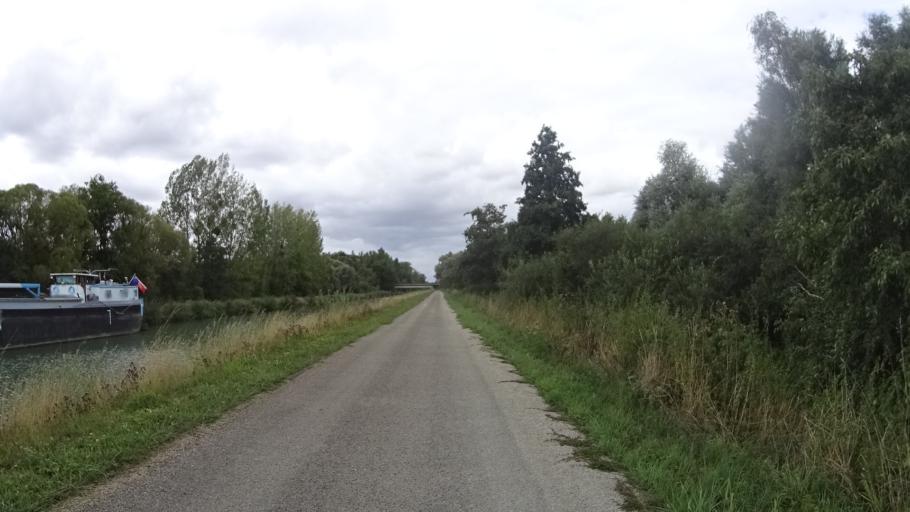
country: FR
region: Picardie
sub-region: Departement de l'Aisne
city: La Fere
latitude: 49.6680
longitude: 3.3537
